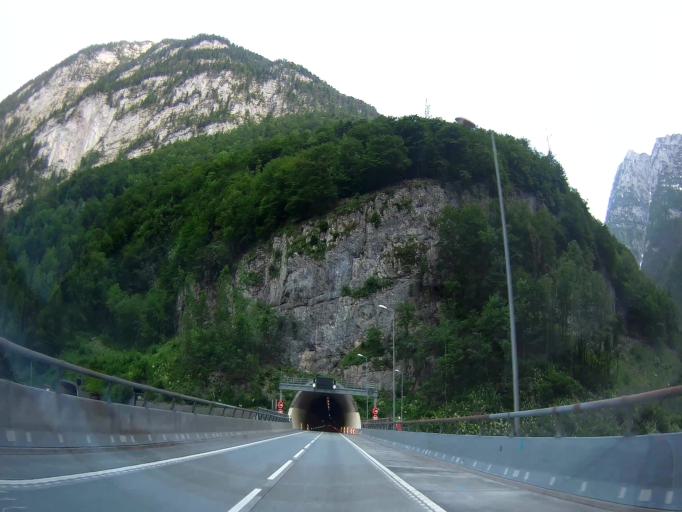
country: AT
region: Salzburg
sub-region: Politischer Bezirk Hallein
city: Golling an der Salzach
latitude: 47.5696
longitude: 13.1682
